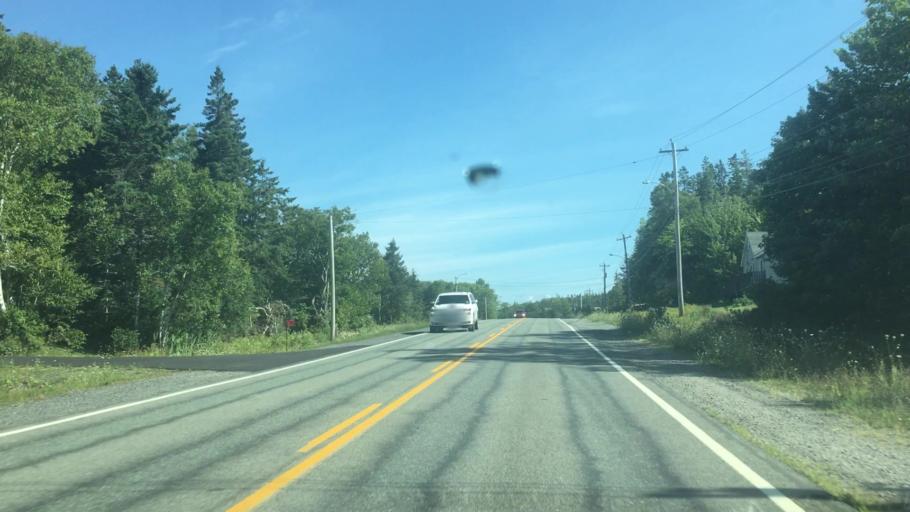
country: CA
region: Nova Scotia
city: Sydney
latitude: 45.9947
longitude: -60.4077
